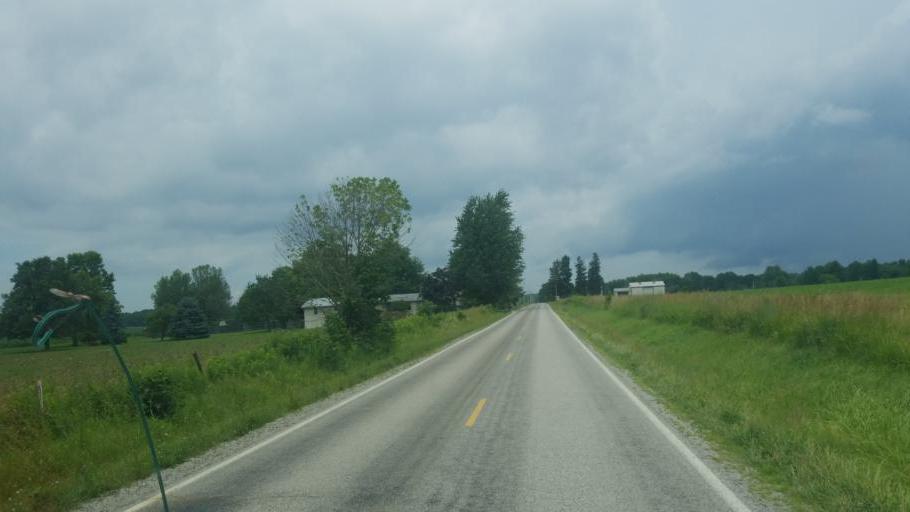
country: US
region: Ohio
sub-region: Wayne County
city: Wooster
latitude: 40.8899
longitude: -81.9535
